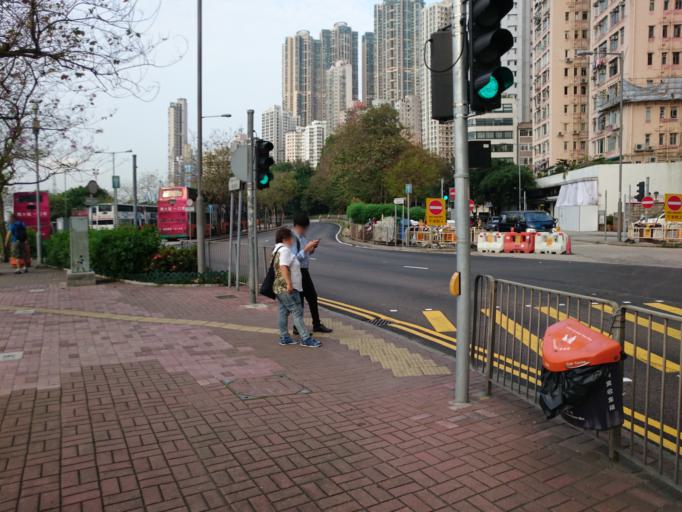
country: HK
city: Hong Kong
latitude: 22.2840
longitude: 114.1277
